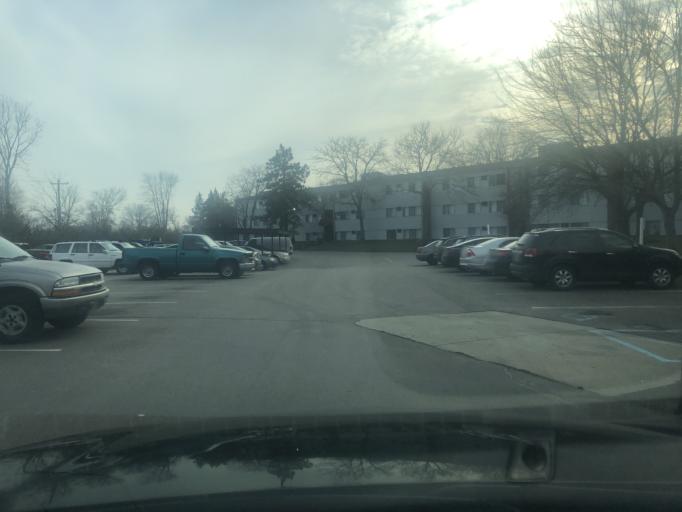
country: US
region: Michigan
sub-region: Wayne County
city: Belleville
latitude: 42.2170
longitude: -83.4895
